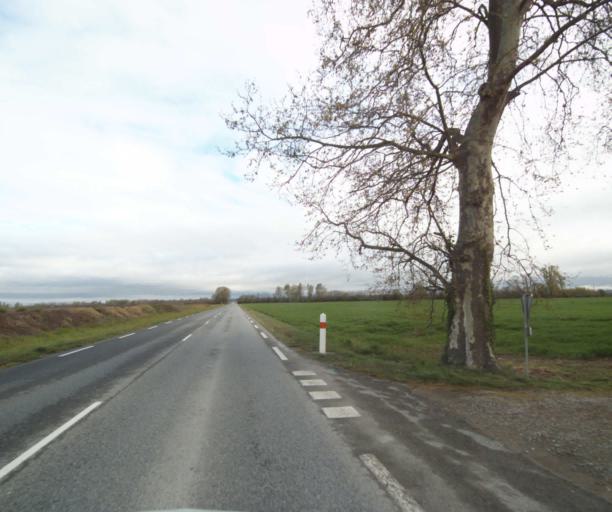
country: FR
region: Midi-Pyrenees
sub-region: Departement de l'Ariege
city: Saverdun
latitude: 43.2133
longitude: 1.6079
